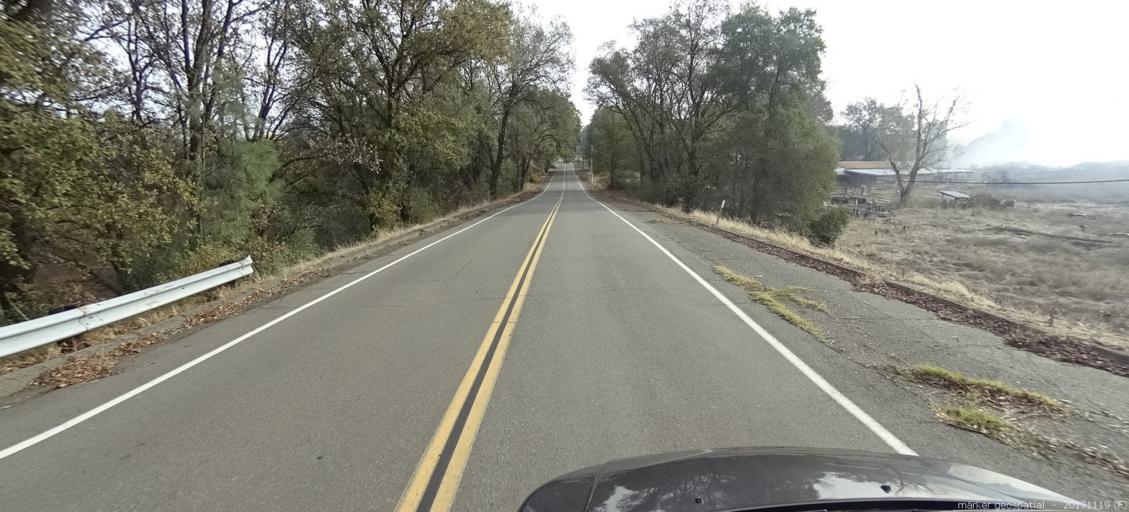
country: US
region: California
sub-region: Shasta County
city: Redding
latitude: 40.5201
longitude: -122.3447
